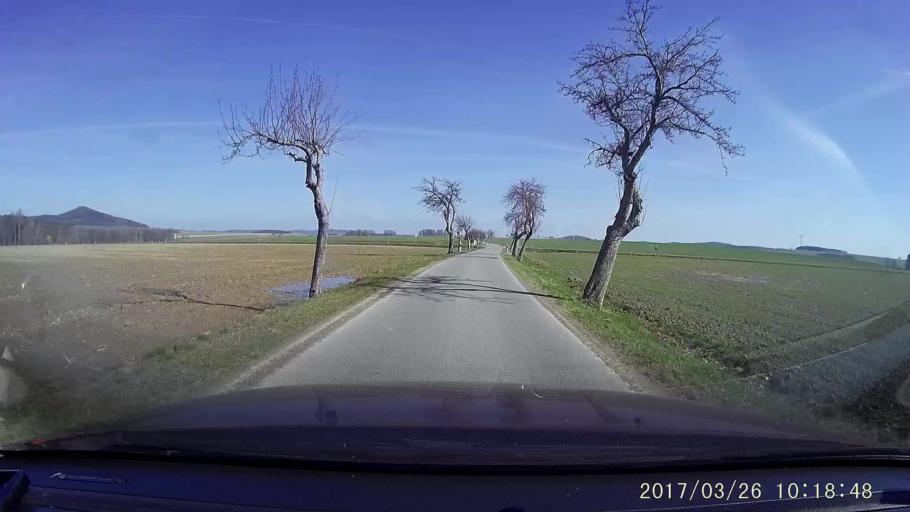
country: DE
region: Saxony
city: Sohland am Rotstein
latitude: 51.0742
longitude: 14.7712
